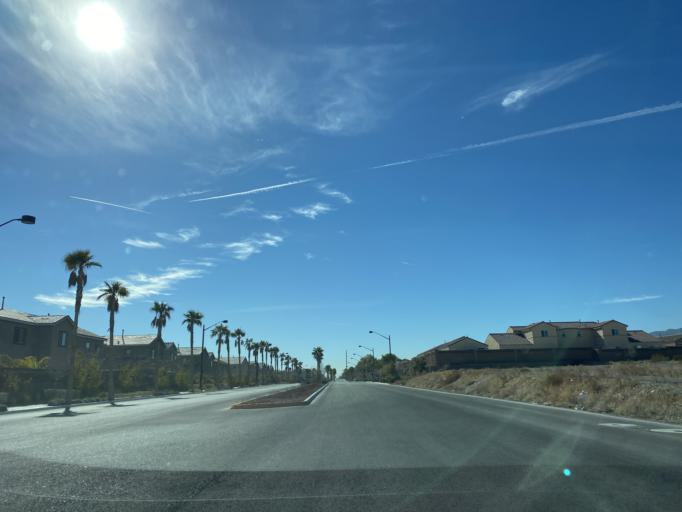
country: US
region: Nevada
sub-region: Clark County
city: Summerlin South
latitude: 36.3055
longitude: -115.2968
